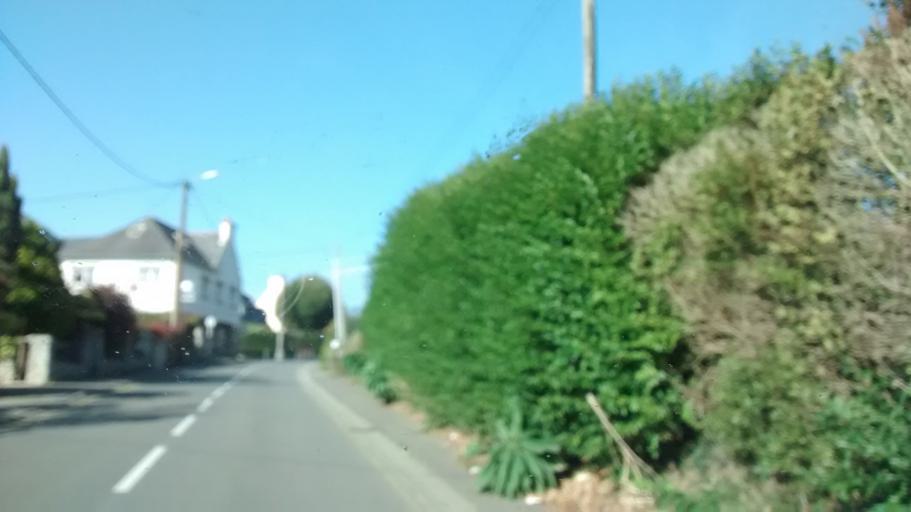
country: FR
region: Brittany
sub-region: Departement des Cotes-d'Armor
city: Trebeurden
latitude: 48.7661
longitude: -3.5618
